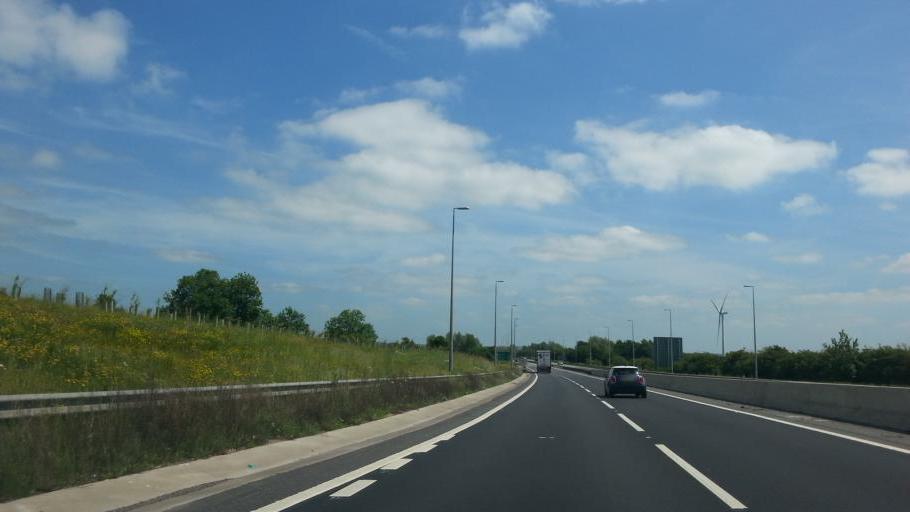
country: GB
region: England
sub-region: Leicestershire
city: Lutterworth
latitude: 52.4016
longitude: -1.1677
